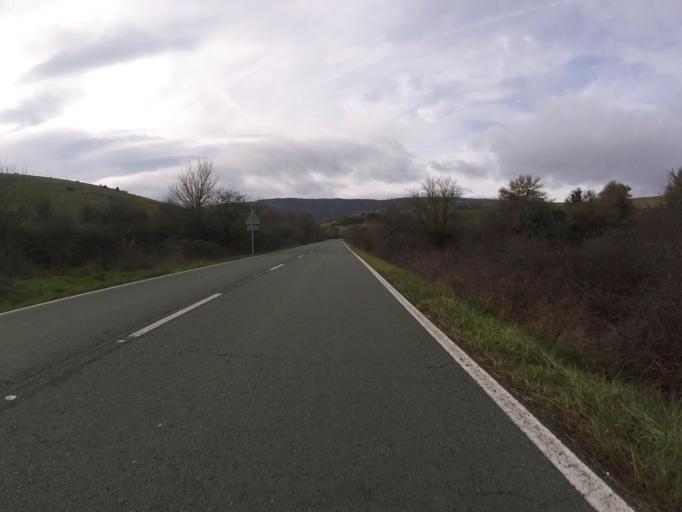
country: ES
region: Navarre
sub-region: Provincia de Navarra
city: Lezaun
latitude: 42.8426
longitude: -2.0165
